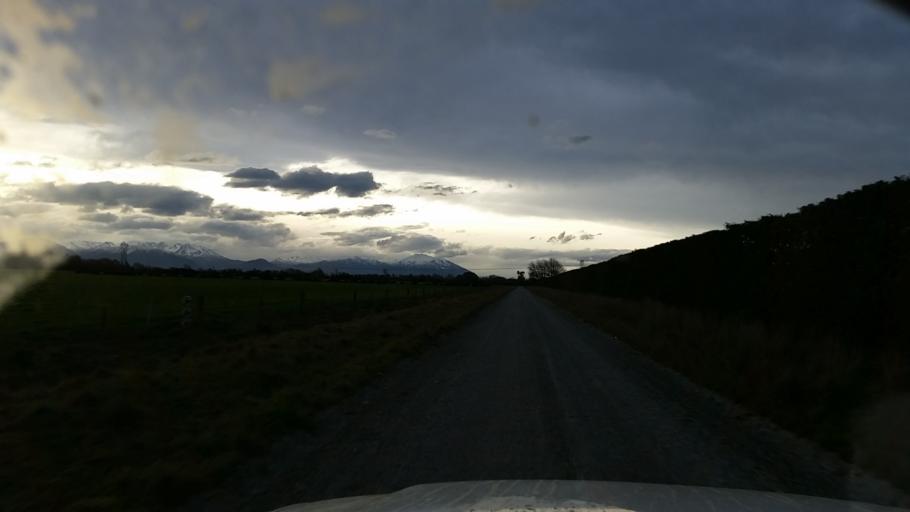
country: NZ
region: Canterbury
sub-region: Ashburton District
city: Ashburton
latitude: -43.8563
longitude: 171.6623
